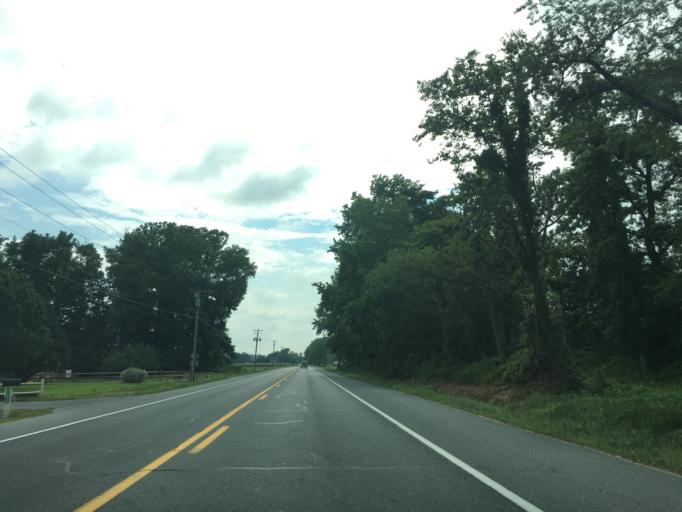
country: US
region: Delaware
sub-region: Sussex County
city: Long Neck
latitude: 38.5556
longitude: -75.1746
